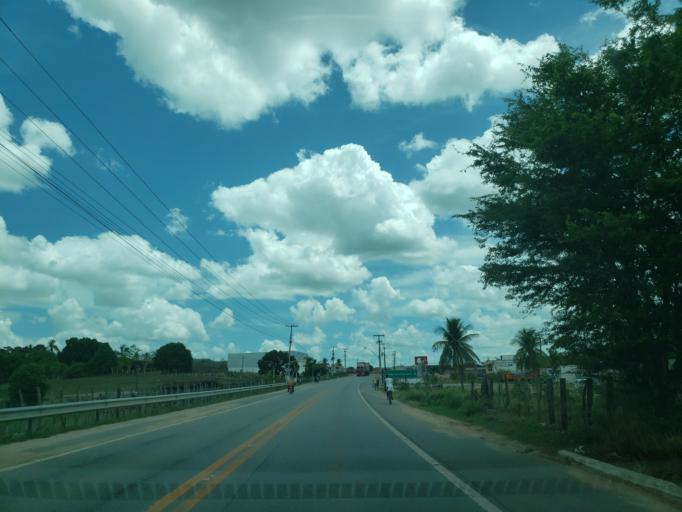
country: BR
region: Alagoas
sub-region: Uniao Dos Palmares
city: Uniao dos Palmares
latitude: -9.1551
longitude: -36.0131
